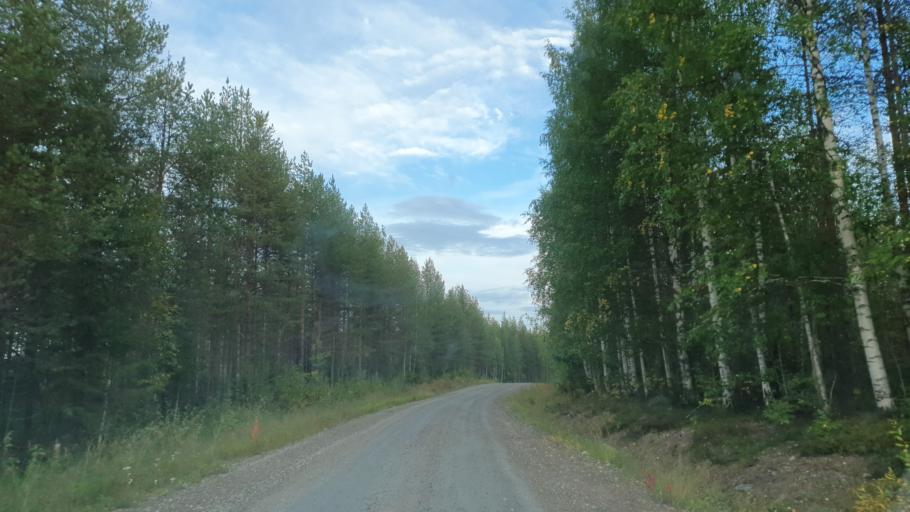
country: FI
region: Kainuu
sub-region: Kehys-Kainuu
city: Kuhmo
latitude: 64.3704
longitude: 29.5610
